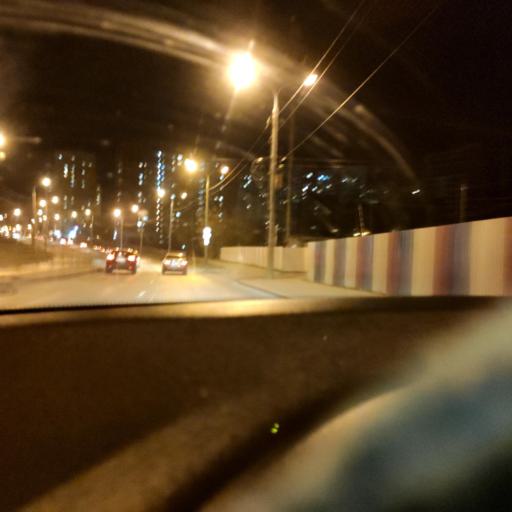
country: RU
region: Samara
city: Samara
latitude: 53.2579
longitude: 50.2046
